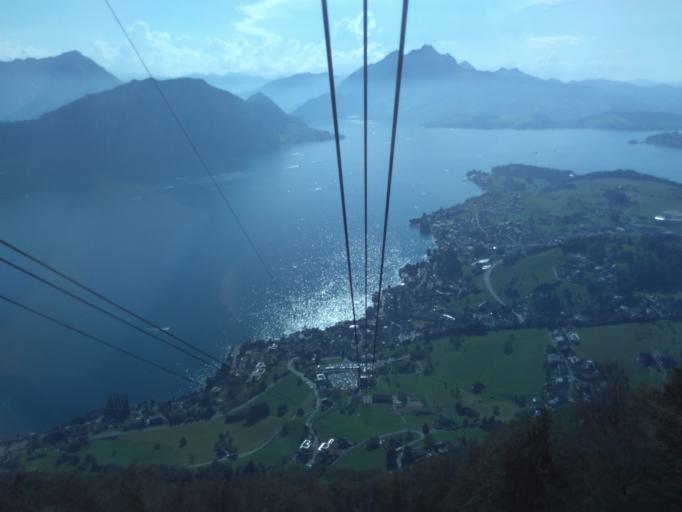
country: CH
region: Lucerne
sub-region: Lucerne-Land District
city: Weggis
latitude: 47.0384
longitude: 8.4519
